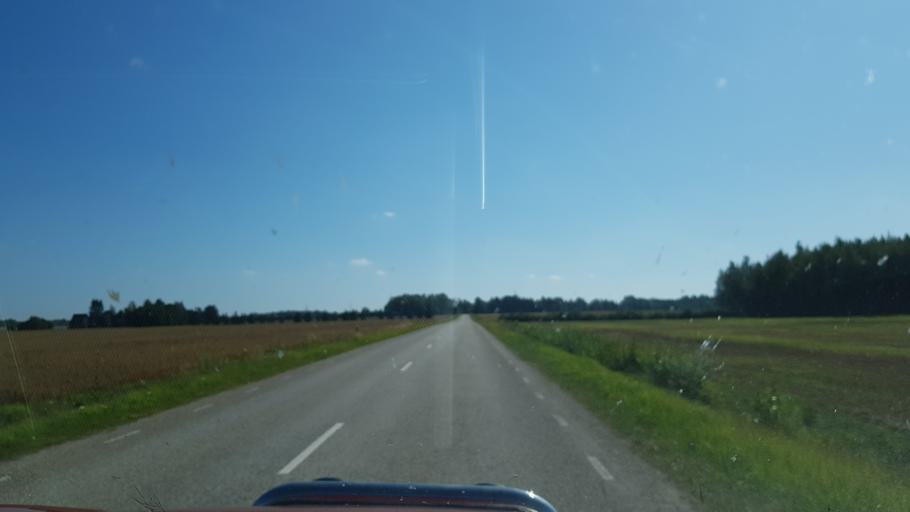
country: EE
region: Polvamaa
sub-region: Polva linn
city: Polva
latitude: 58.2162
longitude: 27.2430
